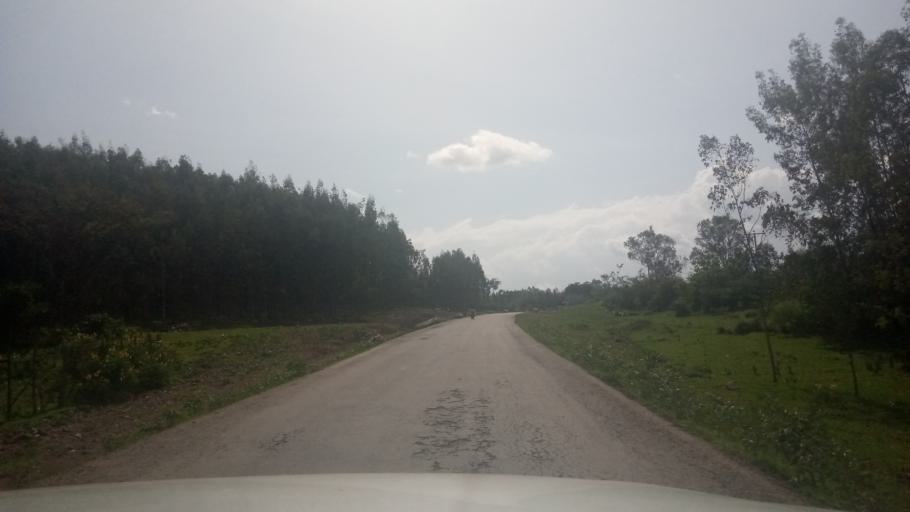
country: ET
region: Oromiya
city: Agaro
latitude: 7.9964
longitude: 36.5020
